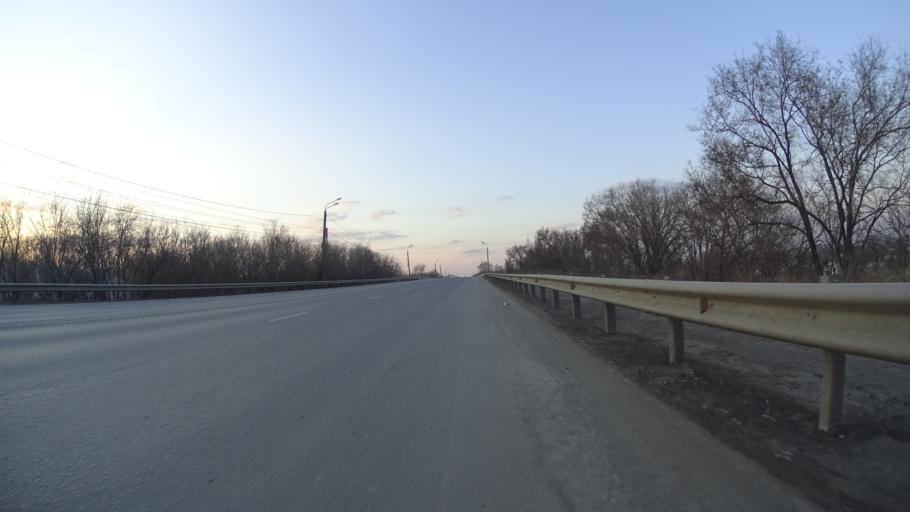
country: RU
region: Chelyabinsk
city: Novosineglazovskiy
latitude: 55.1006
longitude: 61.3878
